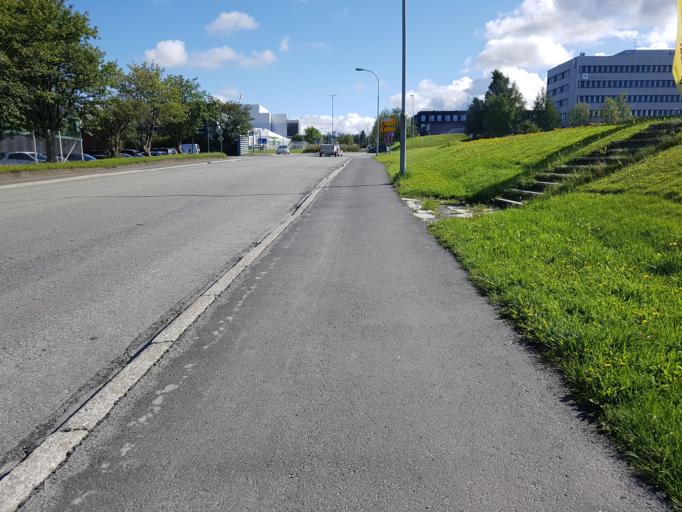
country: NO
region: Sor-Trondelag
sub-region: Trondheim
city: Trondheim
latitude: 63.4249
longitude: 10.4650
